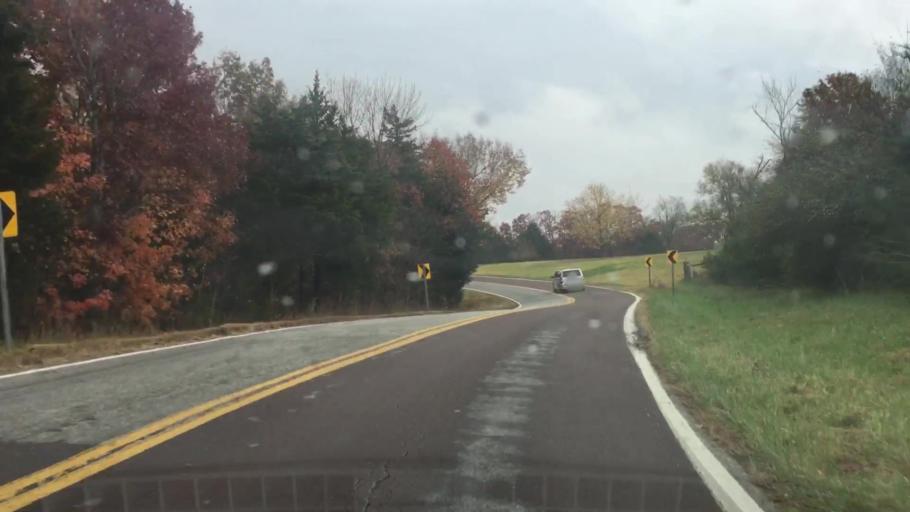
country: US
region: Missouri
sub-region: Callaway County
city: Fulton
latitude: 38.7786
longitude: -91.8367
